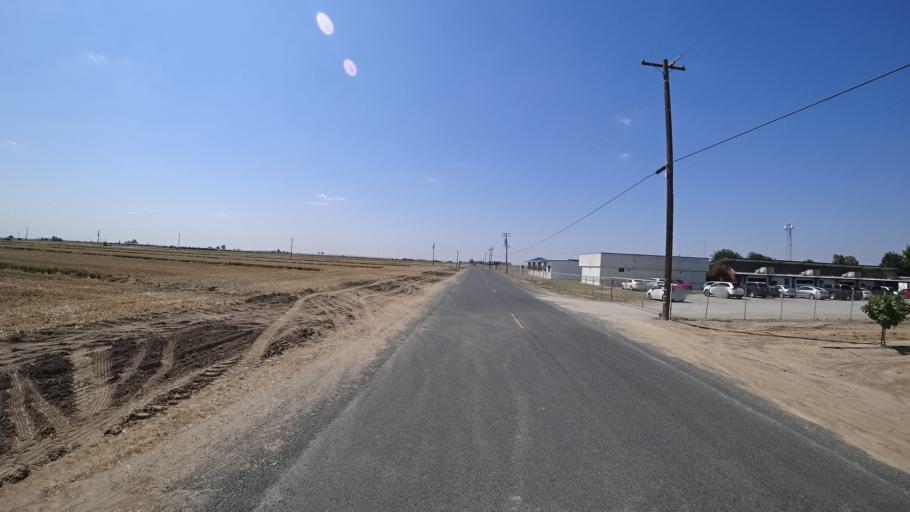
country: US
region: California
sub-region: Kings County
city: Home Garden
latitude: 36.2418
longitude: -119.6190
